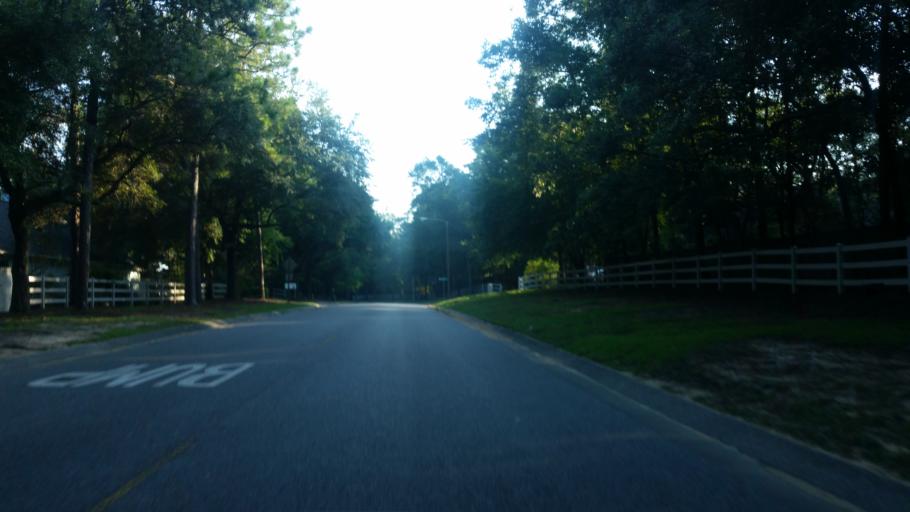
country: US
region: Florida
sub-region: Escambia County
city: Ensley
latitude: 30.5398
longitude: -87.2398
